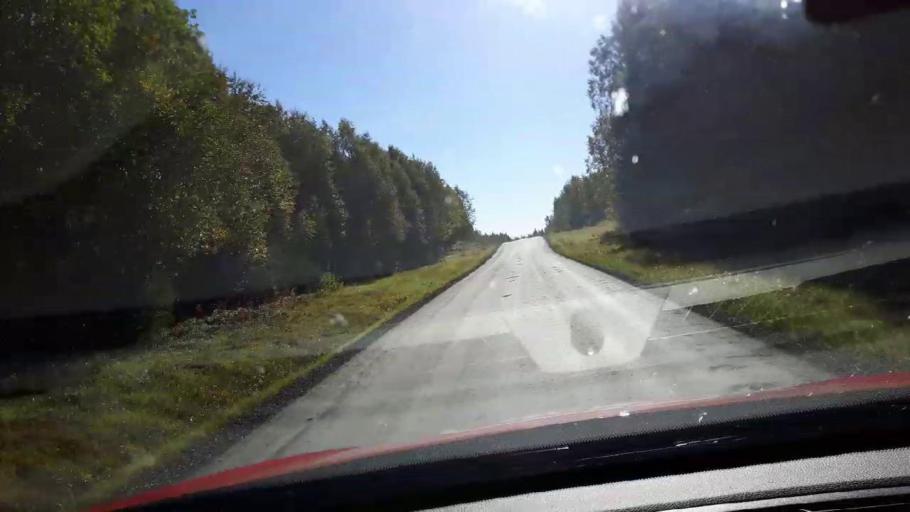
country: NO
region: Nord-Trondelag
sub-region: Lierne
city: Sandvika
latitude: 64.6039
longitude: 13.9662
